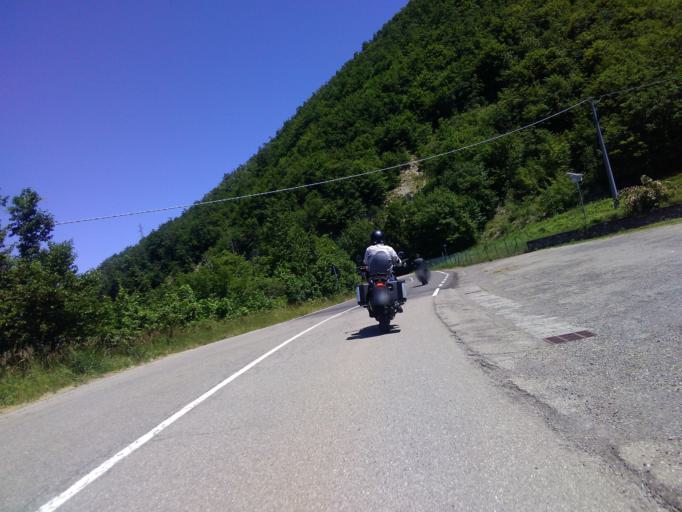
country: IT
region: Emilia-Romagna
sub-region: Provincia di Parma
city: Terenzo
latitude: 44.5676
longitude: 10.0545
